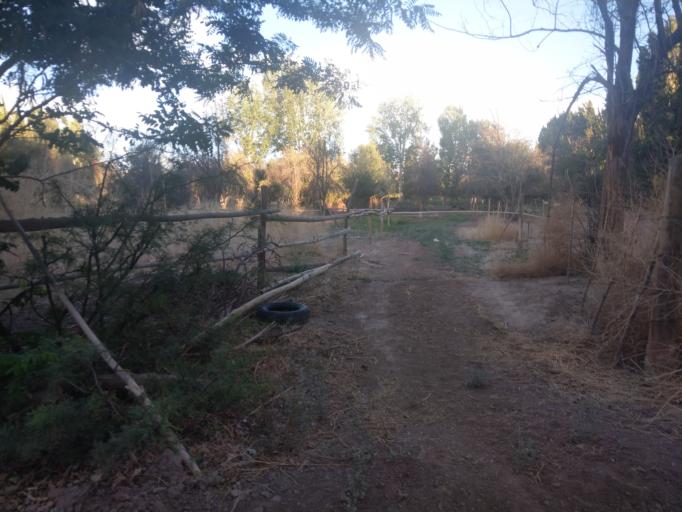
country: AR
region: San Juan
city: Tamberias
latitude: -31.6312
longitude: -69.4627
